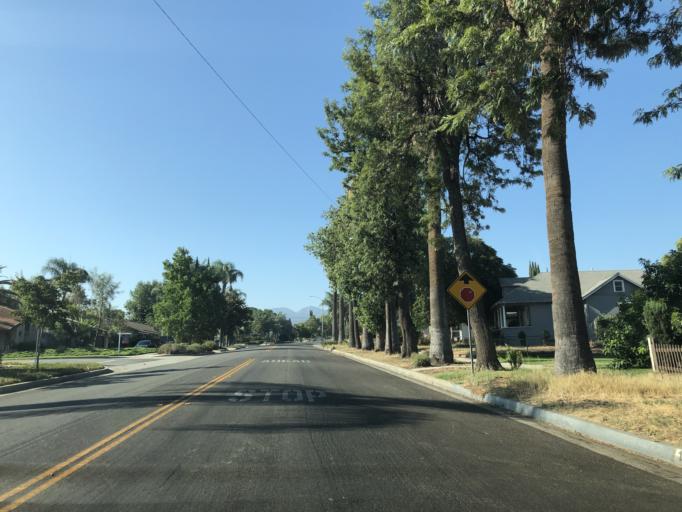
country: US
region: California
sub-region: Riverside County
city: Corona
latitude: 33.8683
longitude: -117.5617
